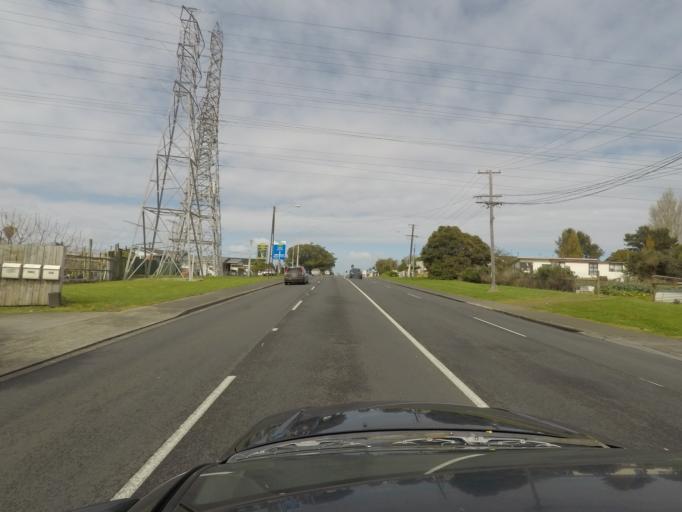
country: NZ
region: Auckland
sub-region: Auckland
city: Tamaki
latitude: -36.9067
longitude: 174.8399
